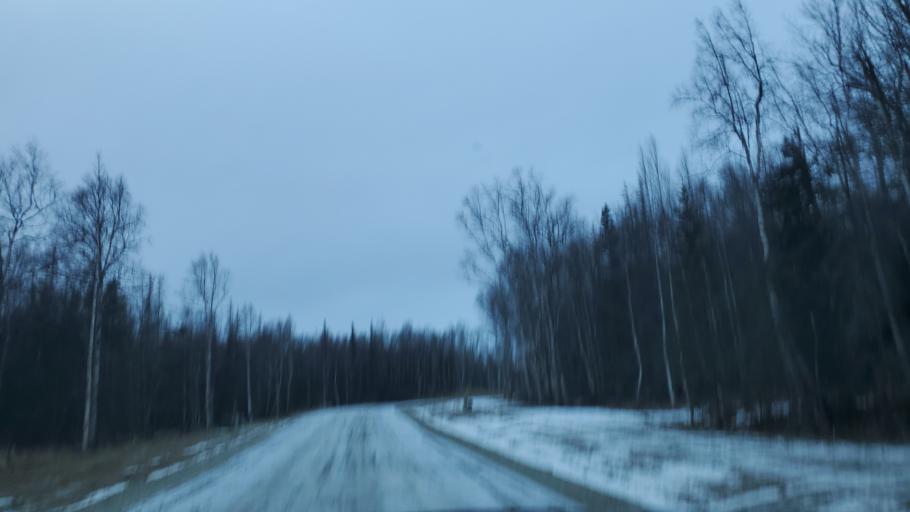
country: US
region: Alaska
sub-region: Matanuska-Susitna Borough
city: Gateway
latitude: 61.6542
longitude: -149.2263
